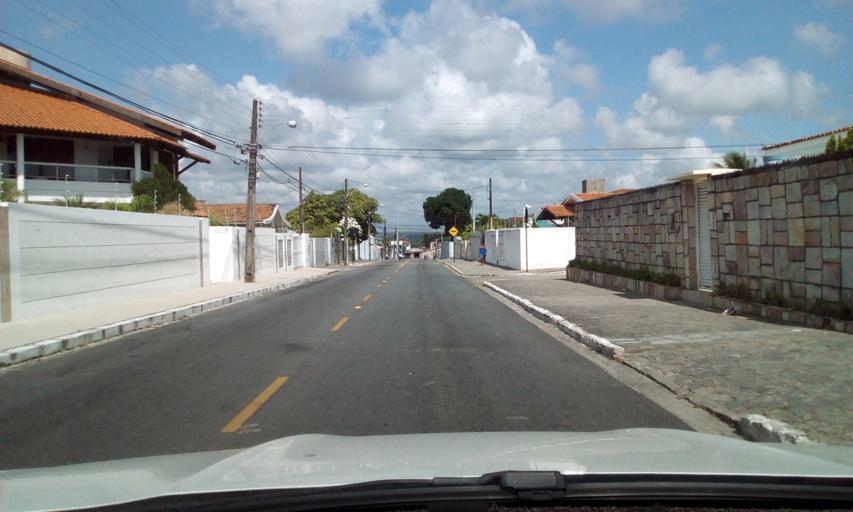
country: BR
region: Paraiba
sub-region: Joao Pessoa
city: Joao Pessoa
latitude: -7.1093
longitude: -34.8672
